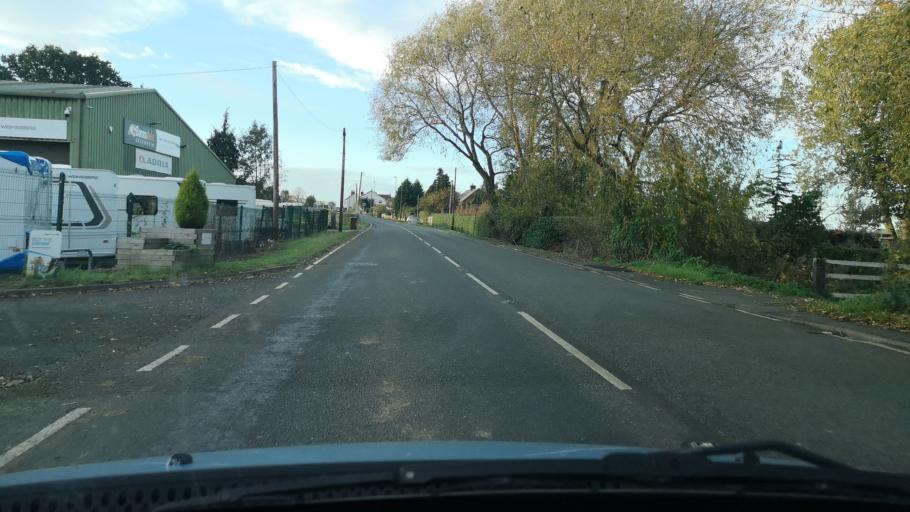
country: GB
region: England
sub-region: City and Borough of Wakefield
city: Badsworth
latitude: 53.6463
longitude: -1.2857
